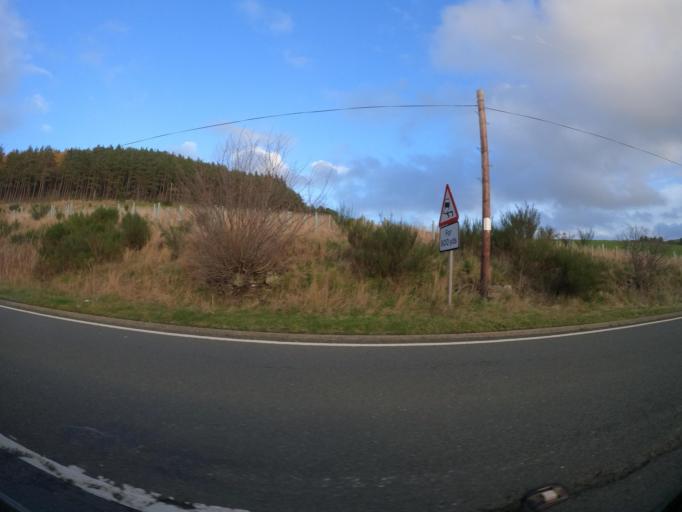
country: GB
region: Scotland
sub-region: Fife
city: Pathhead
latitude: 55.7586
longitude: -2.9245
